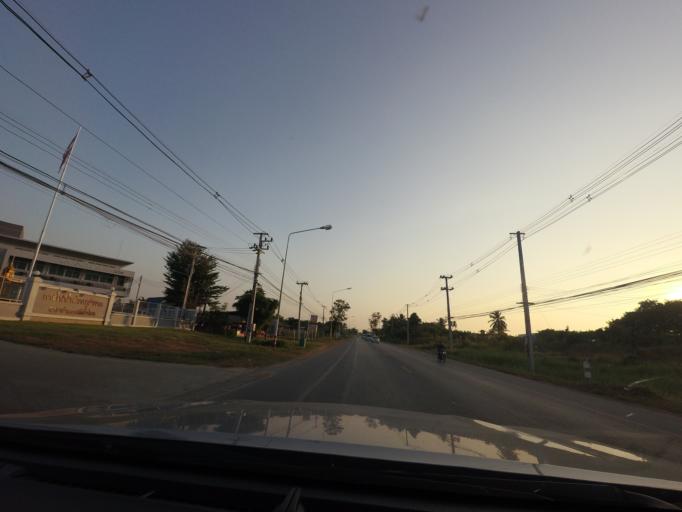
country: TH
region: Sukhothai
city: Si Samrong
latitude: 17.1496
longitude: 99.8526
